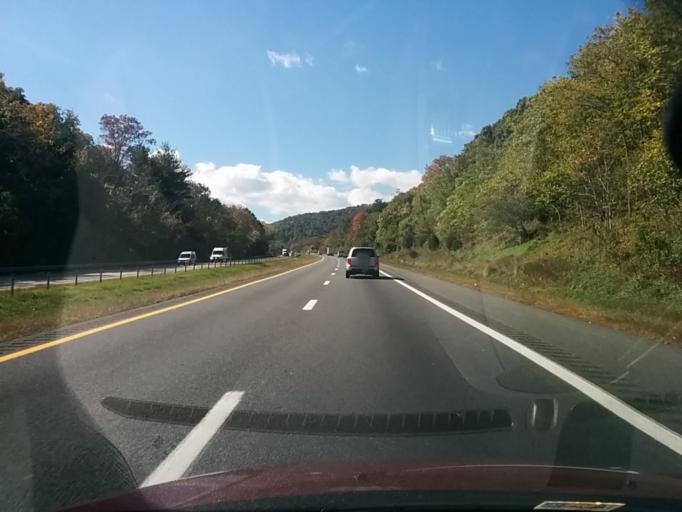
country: US
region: Virginia
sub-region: Albemarle County
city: Crozet
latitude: 38.0475
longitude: -78.7788
